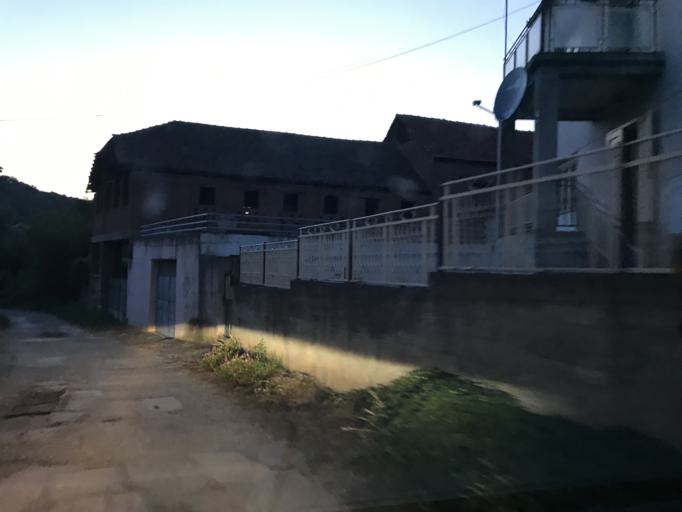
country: BG
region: Vidin
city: Bregovo
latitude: 44.1236
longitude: 22.5674
